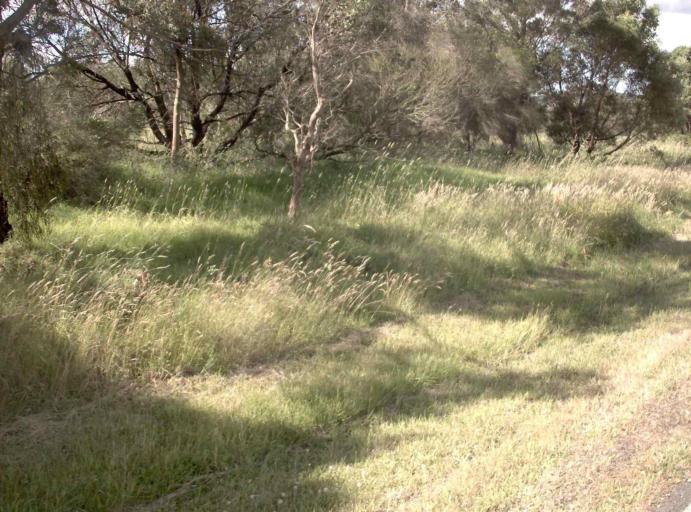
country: AU
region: Victoria
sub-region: Latrobe
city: Morwell
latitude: -38.1689
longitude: 146.4115
